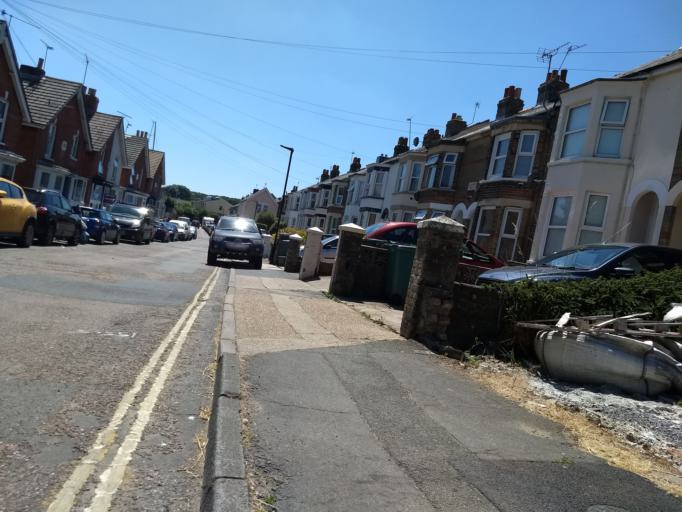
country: GB
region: England
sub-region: Isle of Wight
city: East Cowes
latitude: 50.7562
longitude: -1.2951
